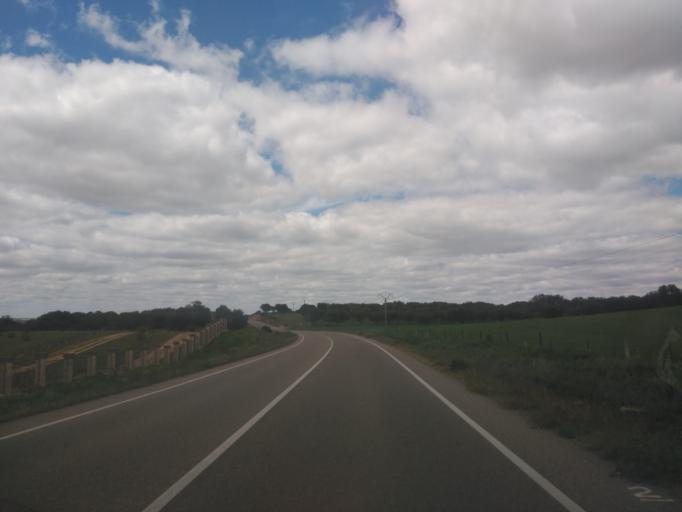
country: ES
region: Castille and Leon
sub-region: Provincia de Salamanca
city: Florida de Liebana
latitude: 41.0369
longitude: -5.7378
